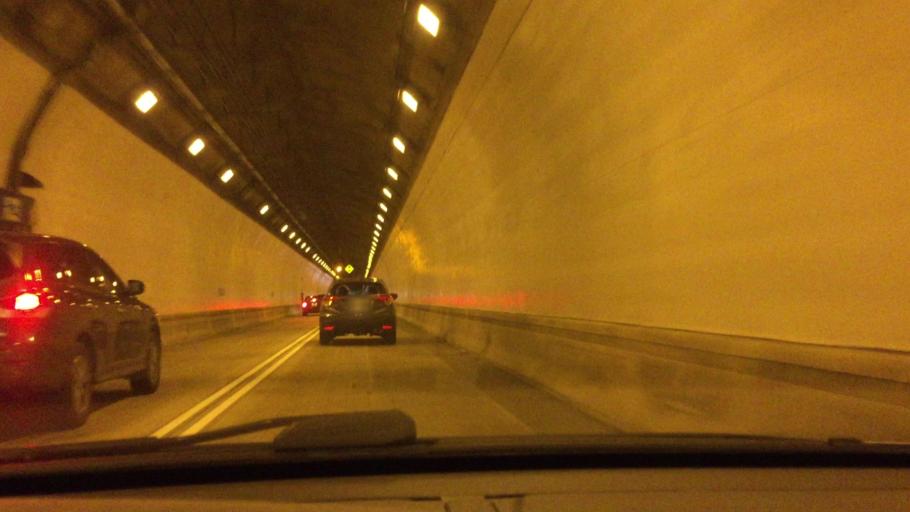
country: US
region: Pennsylvania
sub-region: Allegheny County
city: Mount Oliver
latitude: 40.4222
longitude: -80.0041
